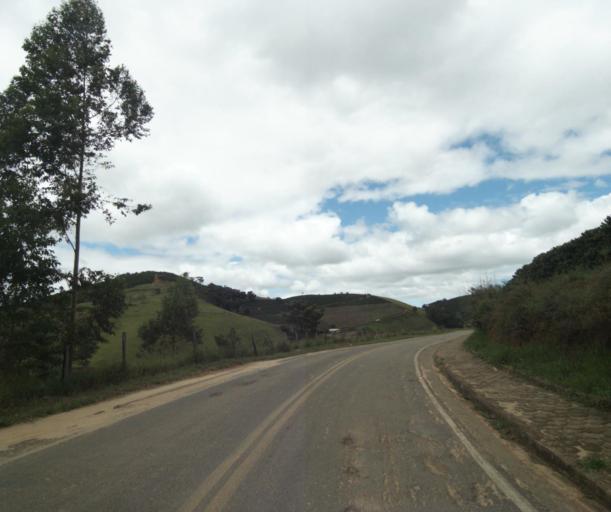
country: BR
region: Espirito Santo
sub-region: Irupi
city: Irupi
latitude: -20.3509
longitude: -41.6266
